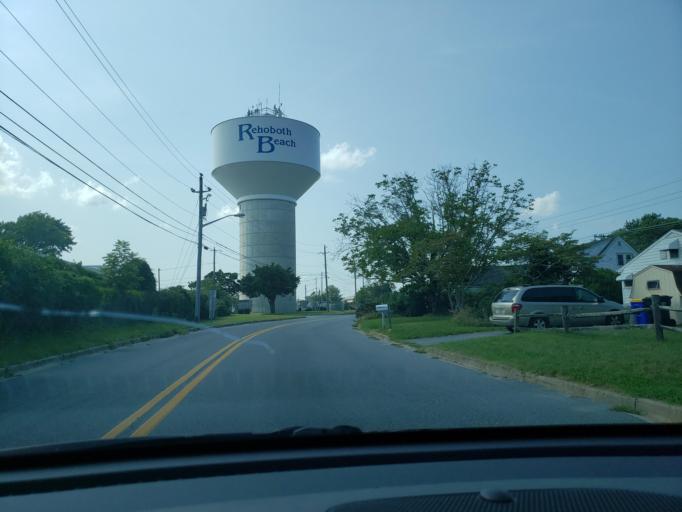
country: US
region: Delaware
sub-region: Sussex County
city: Rehoboth Beach
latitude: 38.7069
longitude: -75.0907
